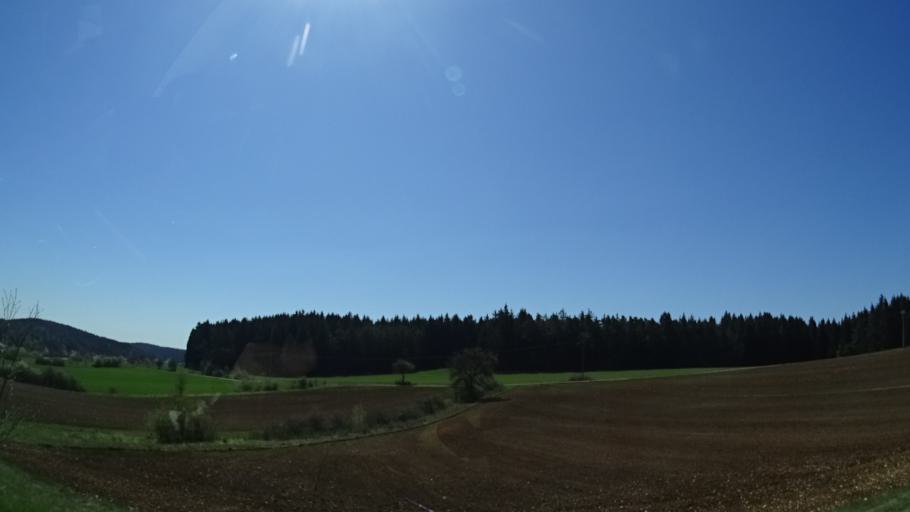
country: DE
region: Bavaria
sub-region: Upper Palatinate
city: Lauterhofen
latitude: 49.4097
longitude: 11.6104
